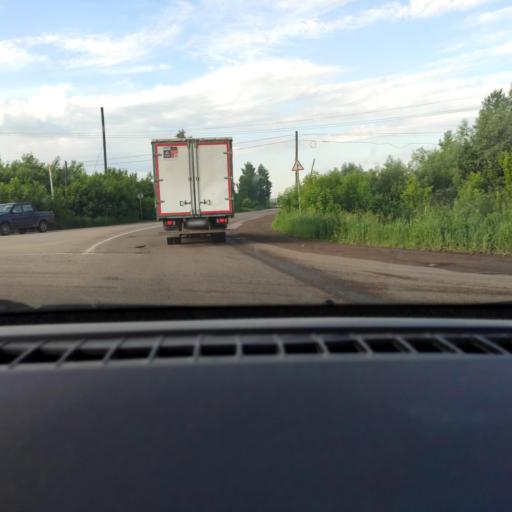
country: RU
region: Udmurtiya
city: Votkinsk
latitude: 57.0429
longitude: 54.0331
